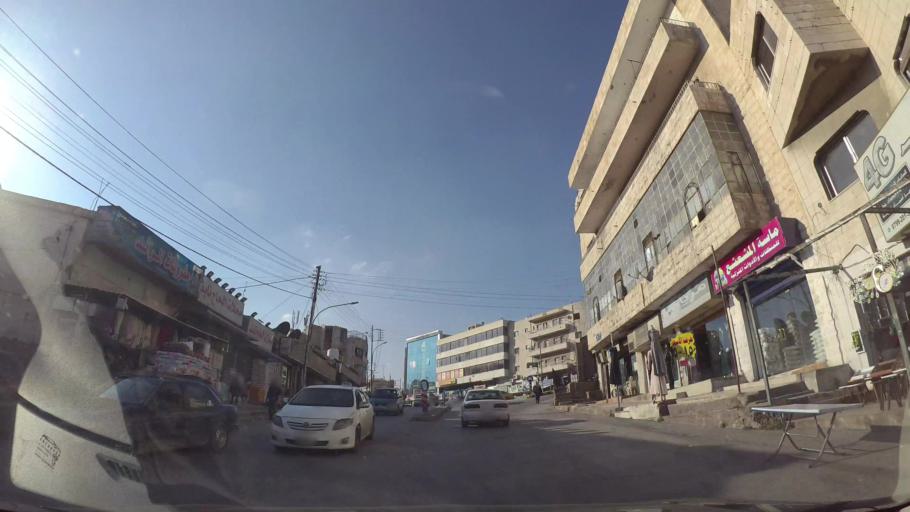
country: JO
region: Amman
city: Amman
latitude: 31.9698
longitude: 35.9592
